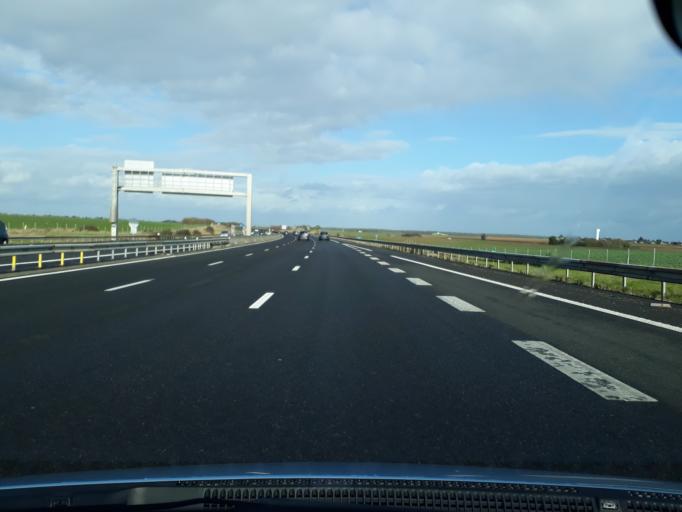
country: FR
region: Centre
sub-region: Departement du Loir-et-Cher
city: La Chaussee-Saint-Victor
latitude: 47.6269
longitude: 1.3497
